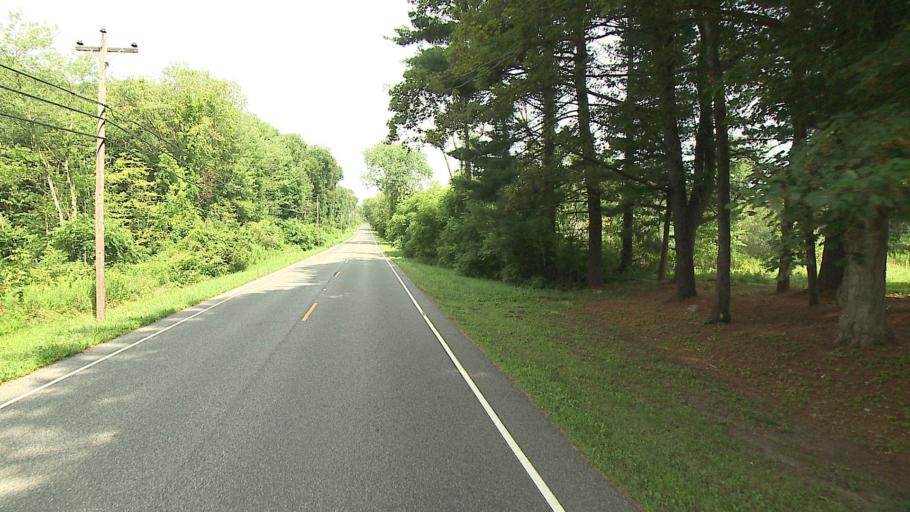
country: US
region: Connecticut
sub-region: Fairfield County
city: Sherman
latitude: 41.6010
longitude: -73.4995
